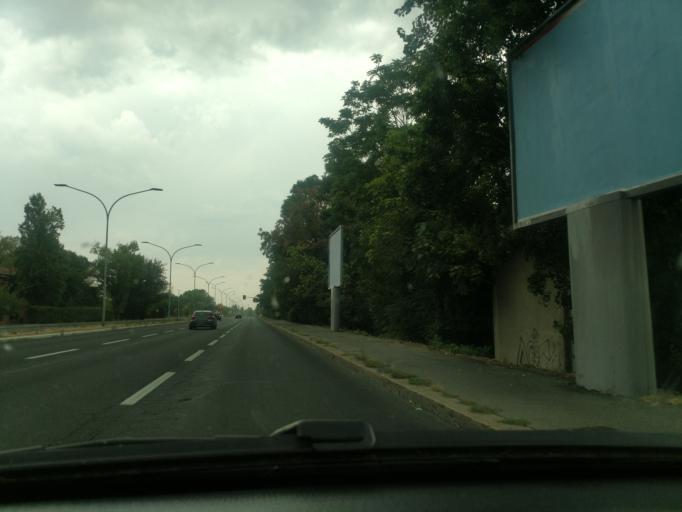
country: IT
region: Emilia-Romagna
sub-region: Provincia di Bologna
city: Casalecchio di Reno
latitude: 44.5041
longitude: 11.2940
